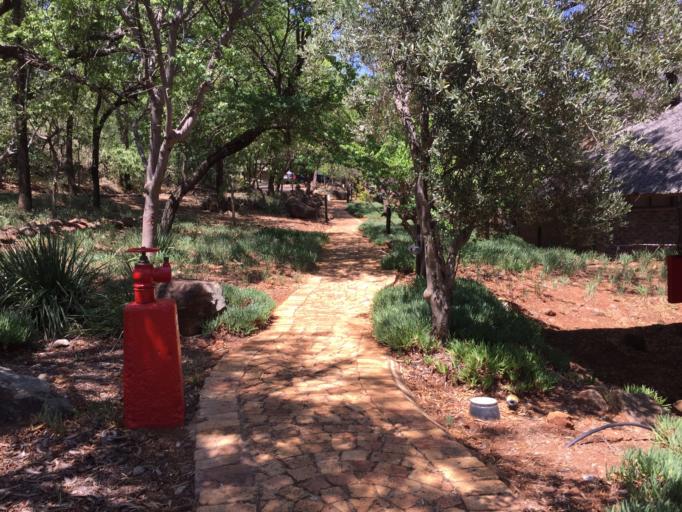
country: ZA
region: North-West
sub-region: Bojanala Platinum District Municipality
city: Mogwase
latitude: -25.3419
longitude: 27.0576
